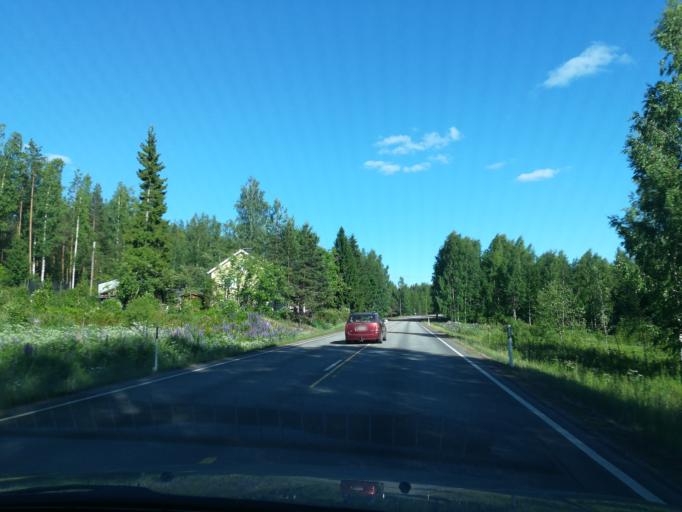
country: FI
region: South Karelia
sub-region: Imatra
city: Ruokolahti
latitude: 61.3719
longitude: 28.6693
